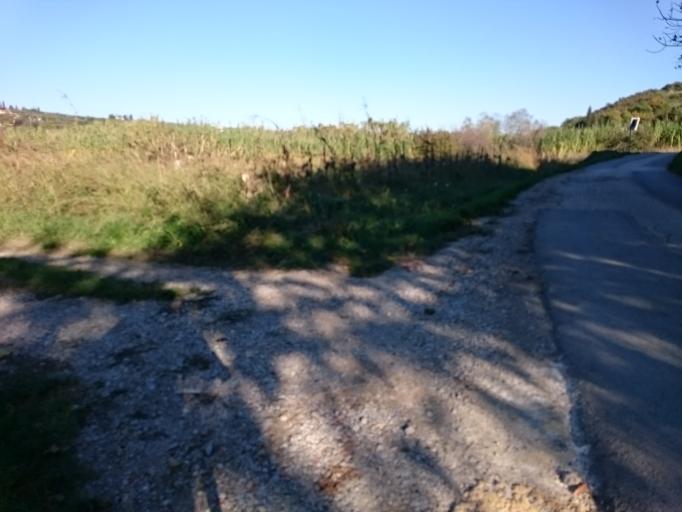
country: SI
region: Piran-Pirano
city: Lucija
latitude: 45.5238
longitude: 13.6175
